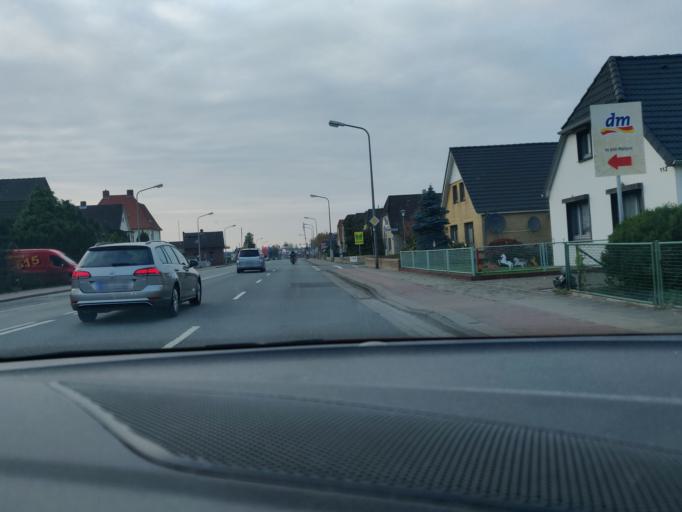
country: DE
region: Lower Saxony
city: Cuxhaven
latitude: 53.8495
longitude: 8.7213
